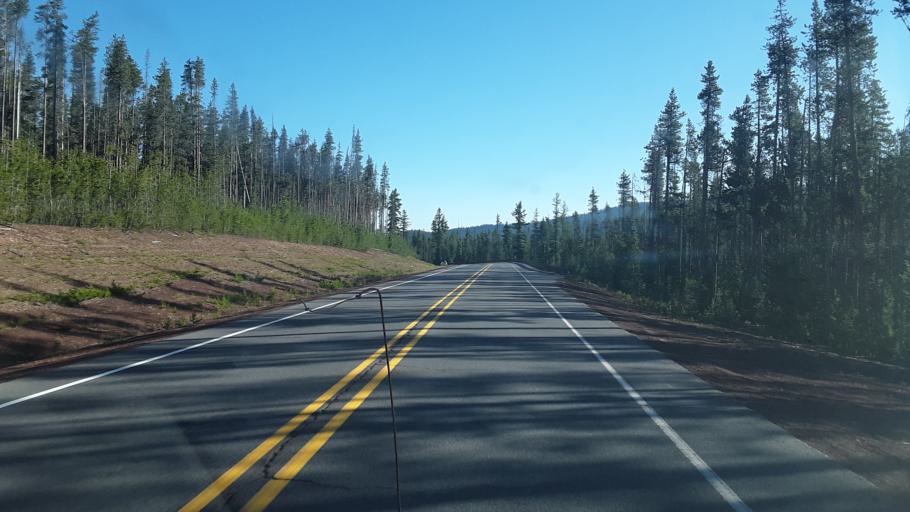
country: US
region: Oregon
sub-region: Lane County
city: Oakridge
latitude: 43.1038
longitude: -122.1299
